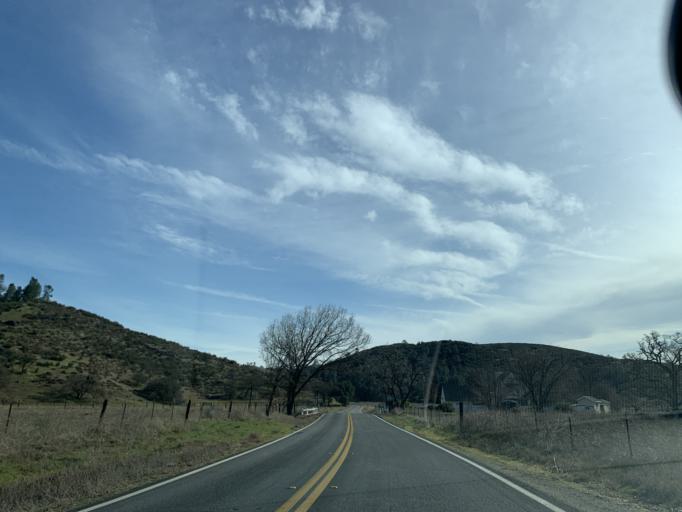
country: US
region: California
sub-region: Monterey County
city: Soledad
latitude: 36.5180
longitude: -121.1368
